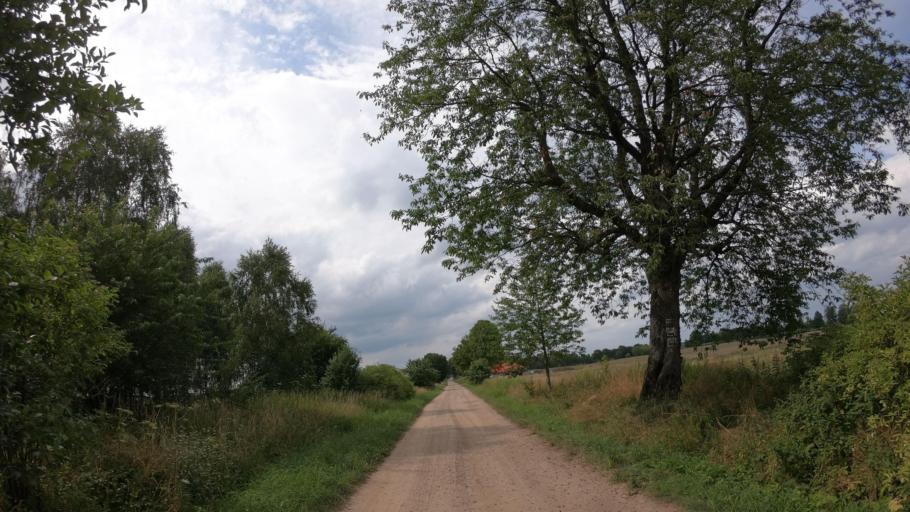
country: PL
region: West Pomeranian Voivodeship
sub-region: Powiat drawski
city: Kalisz Pomorski
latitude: 53.2906
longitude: 15.9299
